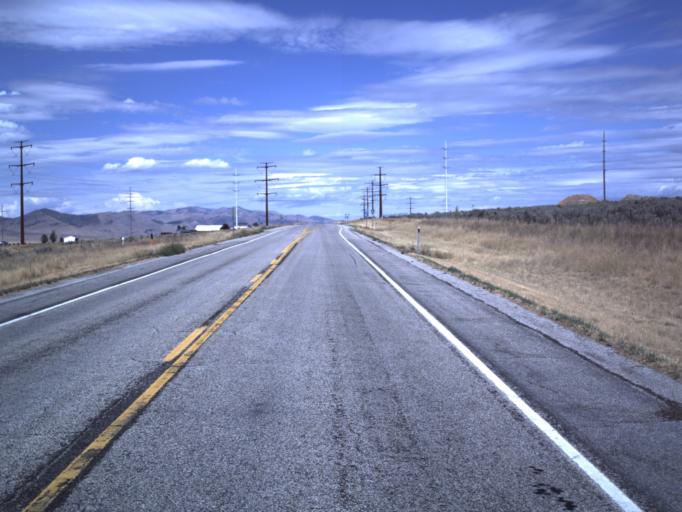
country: US
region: Utah
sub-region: Box Elder County
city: Garland
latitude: 41.8852
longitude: -112.1593
